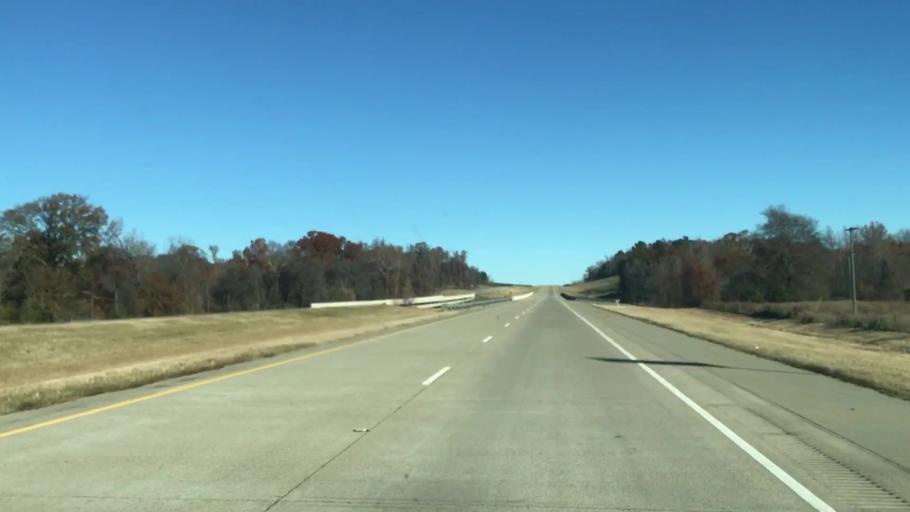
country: US
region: Louisiana
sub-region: Caddo Parish
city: Oil City
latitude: 32.7857
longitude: -93.8884
